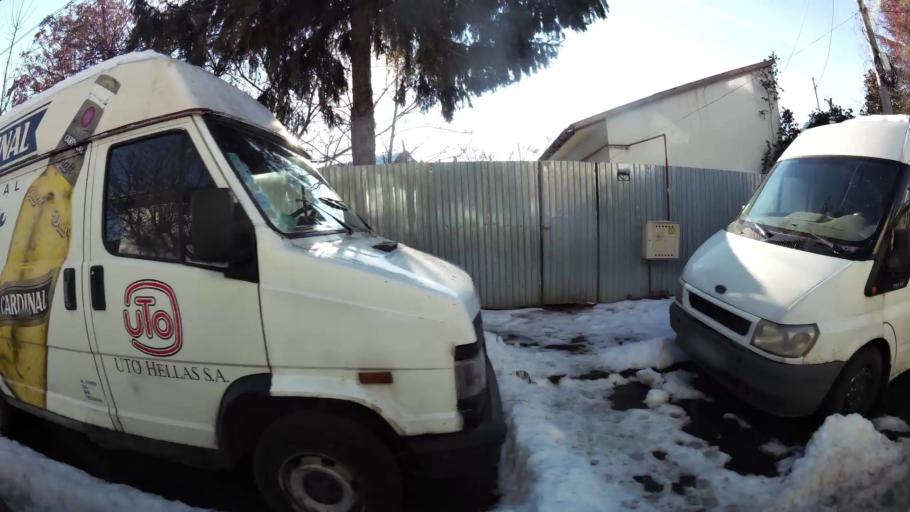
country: RO
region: Bucuresti
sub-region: Municipiul Bucuresti
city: Bucuresti
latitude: 44.4036
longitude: 26.0912
